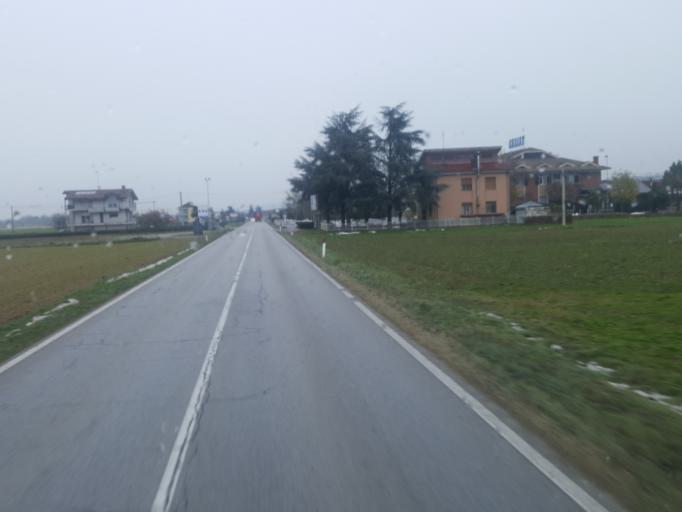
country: IT
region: Piedmont
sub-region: Provincia di Cuneo
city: Breo
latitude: 44.4082
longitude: 7.8367
